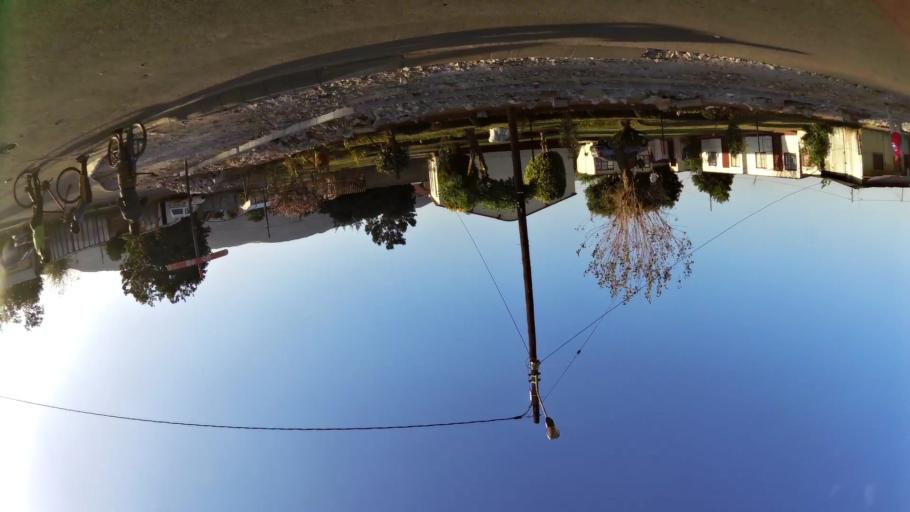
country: ZA
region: North-West
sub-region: Bojanala Platinum District Municipality
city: Rustenburg
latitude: -25.6363
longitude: 27.2116
